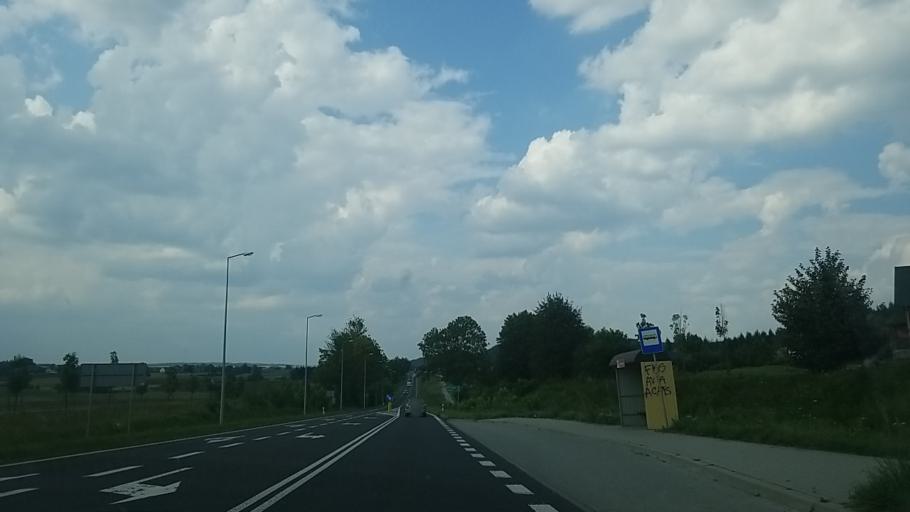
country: PL
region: Lublin Voivodeship
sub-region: Powiat bilgorajski
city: Goraj
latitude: 50.7312
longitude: 22.6674
